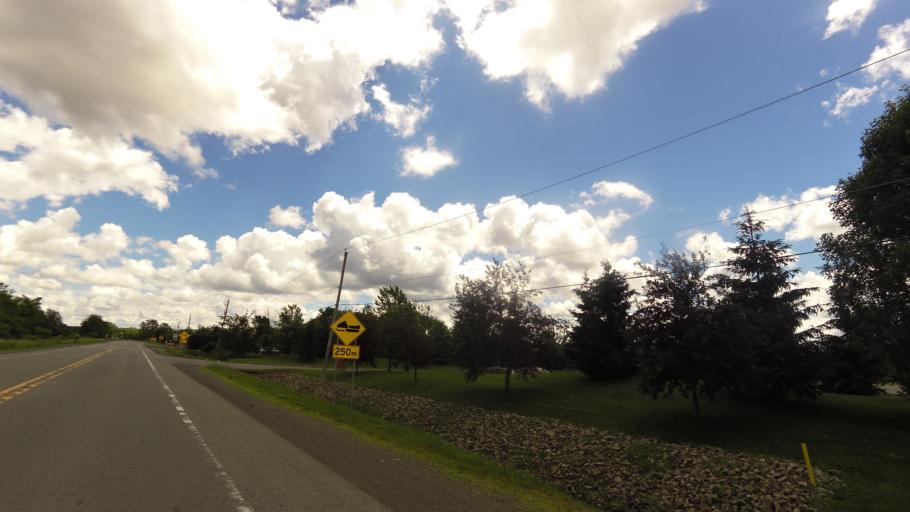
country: CA
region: Quebec
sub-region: Monteregie
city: Hudson
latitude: 45.5292
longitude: -74.2033
